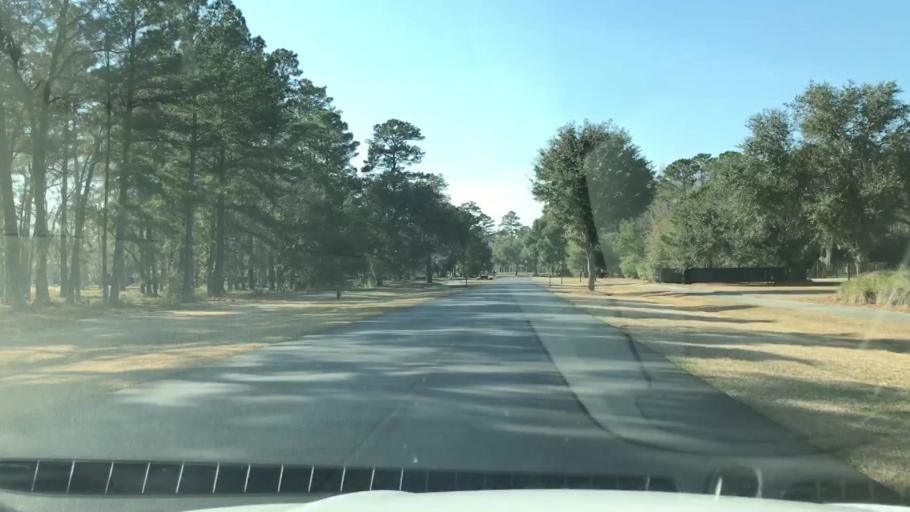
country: US
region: South Carolina
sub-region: Beaufort County
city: Bluffton
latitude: 32.3417
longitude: -80.9147
